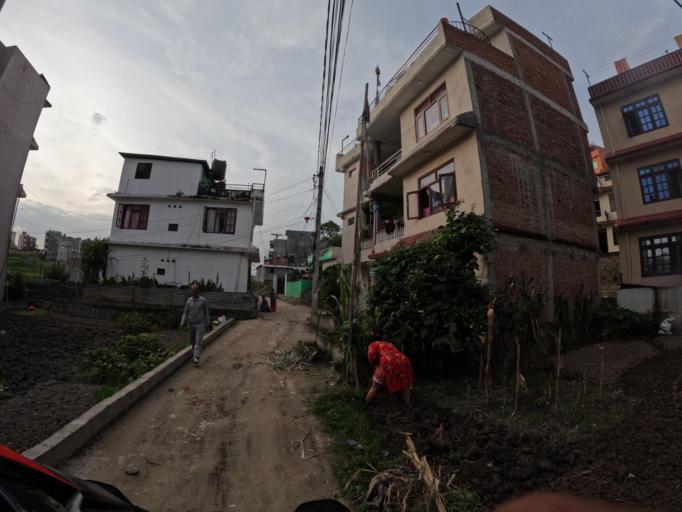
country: NP
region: Central Region
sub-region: Bagmati Zone
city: Bhaktapur
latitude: 27.6839
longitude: 85.3936
